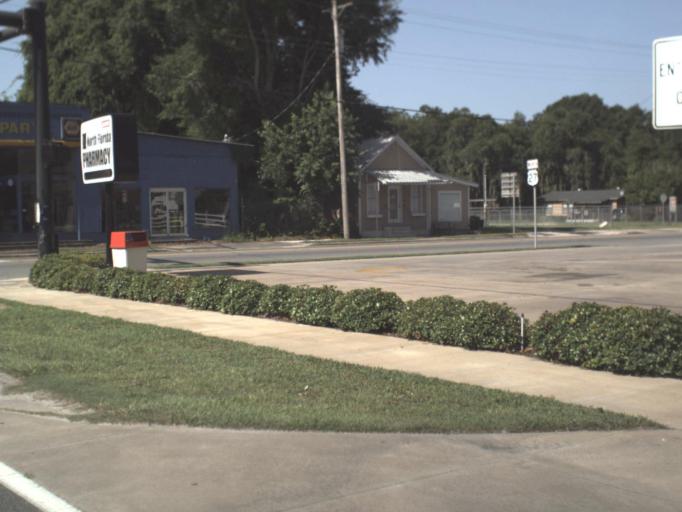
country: US
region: Florida
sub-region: Alachua County
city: High Springs
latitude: 29.9234
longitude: -82.7139
